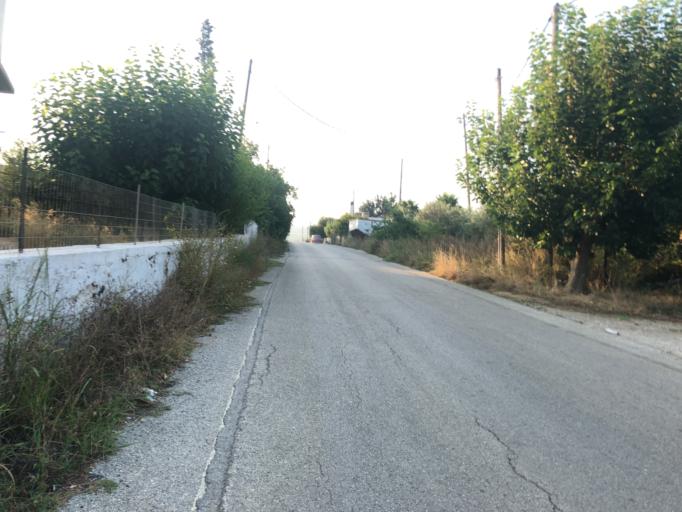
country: GR
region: Crete
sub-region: Nomos Chanias
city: Georgioupolis
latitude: 35.3490
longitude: 24.2842
